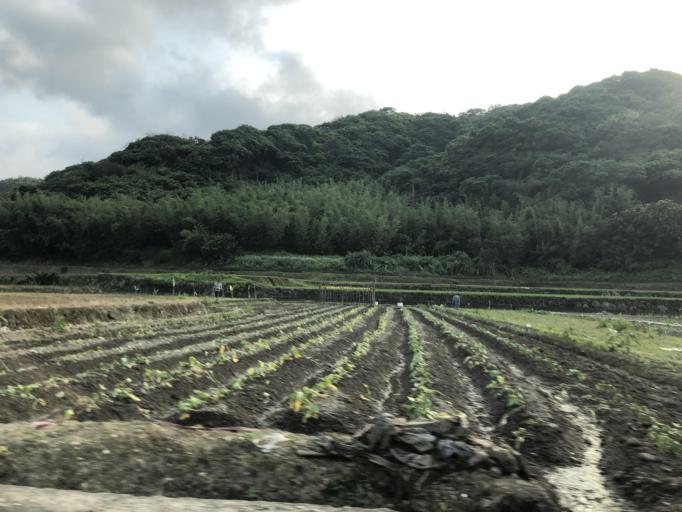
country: TW
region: Taiwan
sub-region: Keelung
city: Keelung
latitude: 25.2081
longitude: 121.6470
